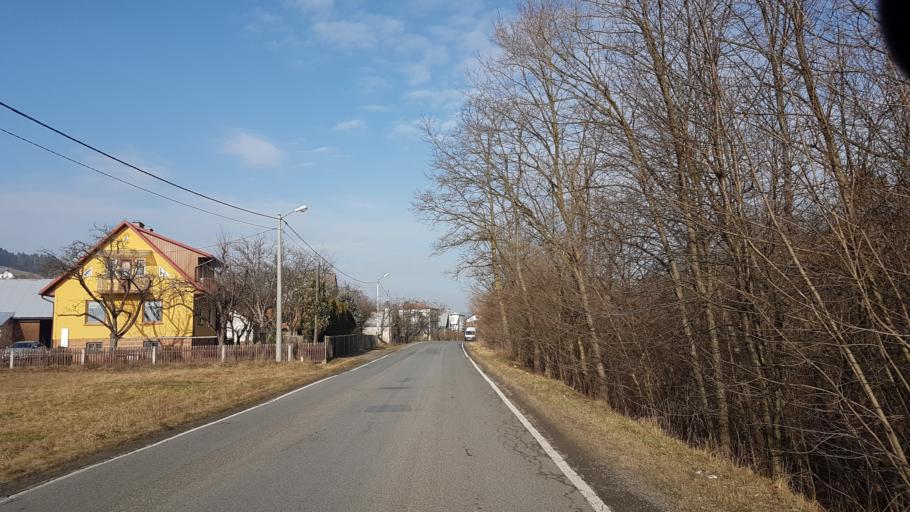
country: PL
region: Lesser Poland Voivodeship
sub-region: Powiat limanowski
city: Lukowica
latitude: 49.6183
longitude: 20.5113
